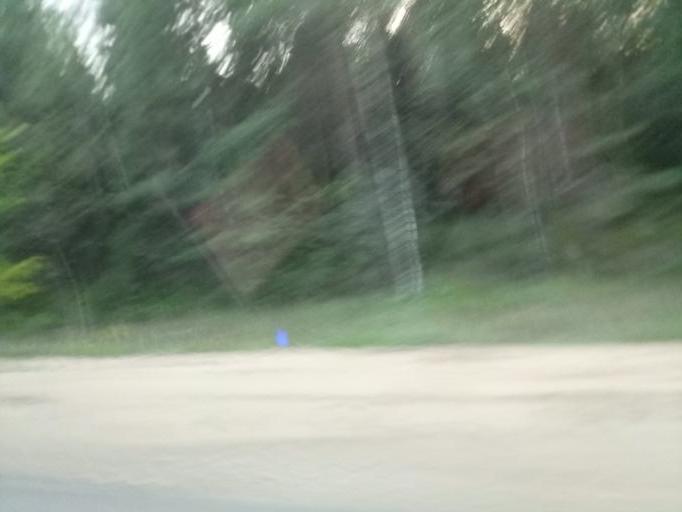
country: RU
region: Moskovskaya
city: Noginsk-9
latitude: 56.0861
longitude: 38.5779
